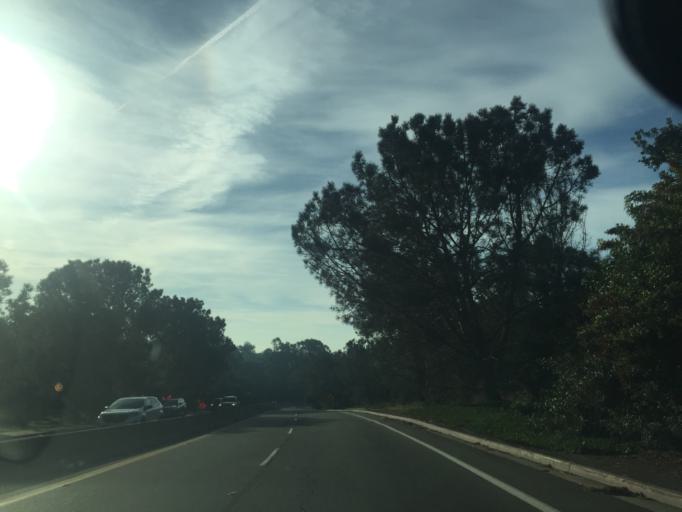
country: US
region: California
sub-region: San Diego County
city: La Jolla
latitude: 32.8646
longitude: -117.2434
